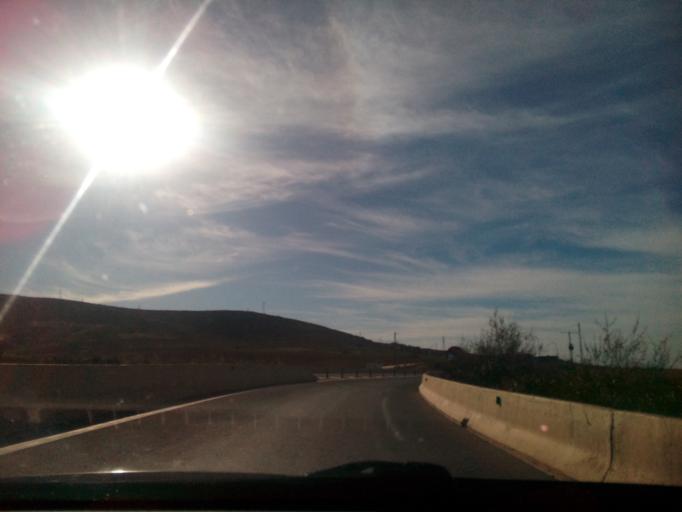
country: DZ
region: Tlemcen
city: Hennaya
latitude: 34.9193
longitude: -1.3704
